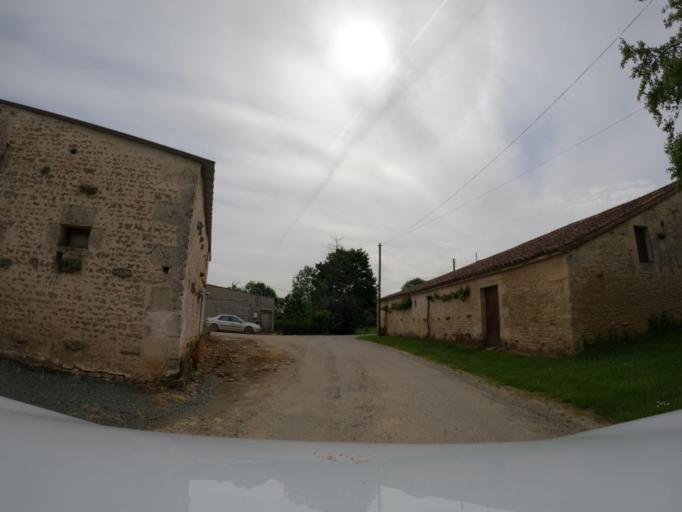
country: FR
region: Pays de la Loire
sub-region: Departement de la Vendee
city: Saint-Hilaire-des-Loges
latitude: 46.5087
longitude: -0.6487
